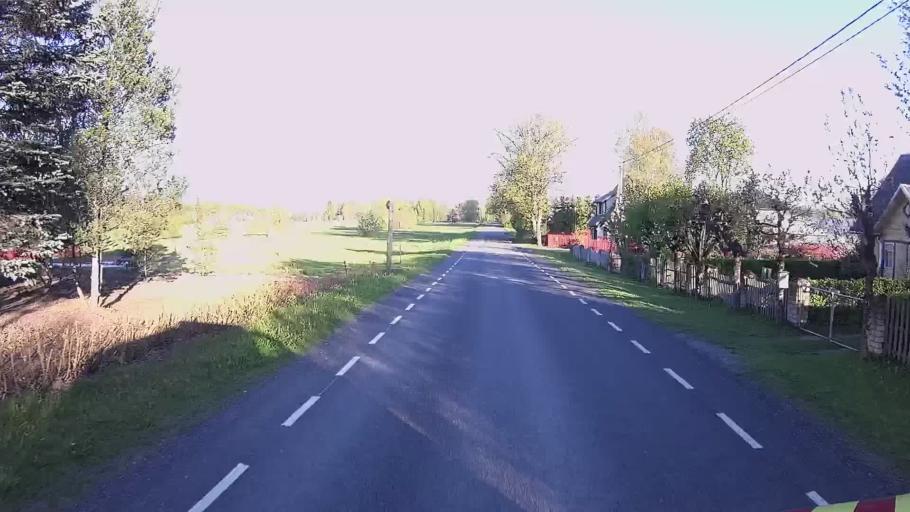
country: EE
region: Jogevamaa
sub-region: Poltsamaa linn
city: Poltsamaa
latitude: 58.5300
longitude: 25.9496
